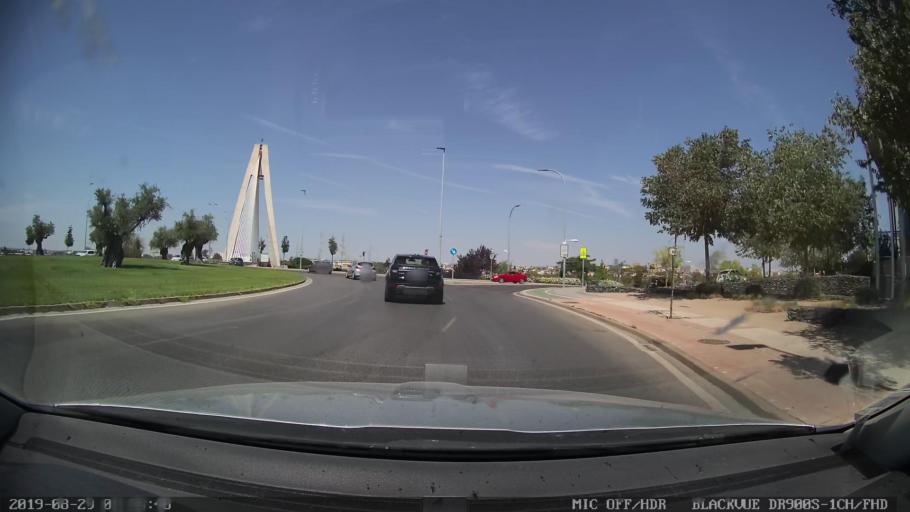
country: ES
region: Extremadura
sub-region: Provincia de Badajoz
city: Badajoz
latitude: 38.8737
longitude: -6.9909
